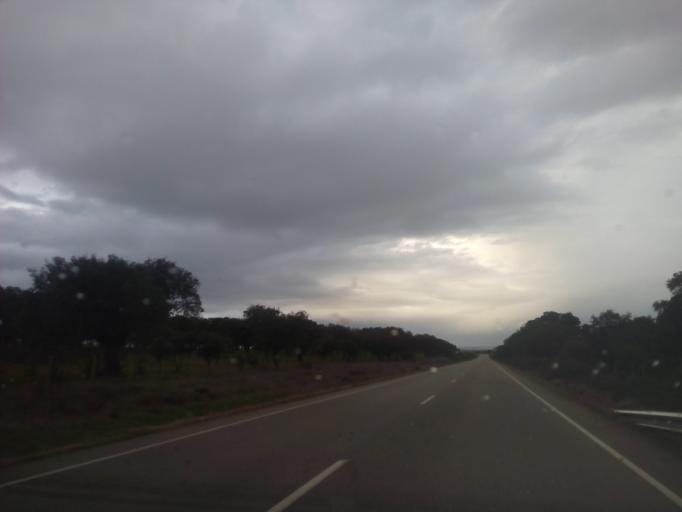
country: ES
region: Castille and Leon
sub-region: Provincia de Salamanca
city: Abusejo
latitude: 40.6880
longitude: -6.1323
